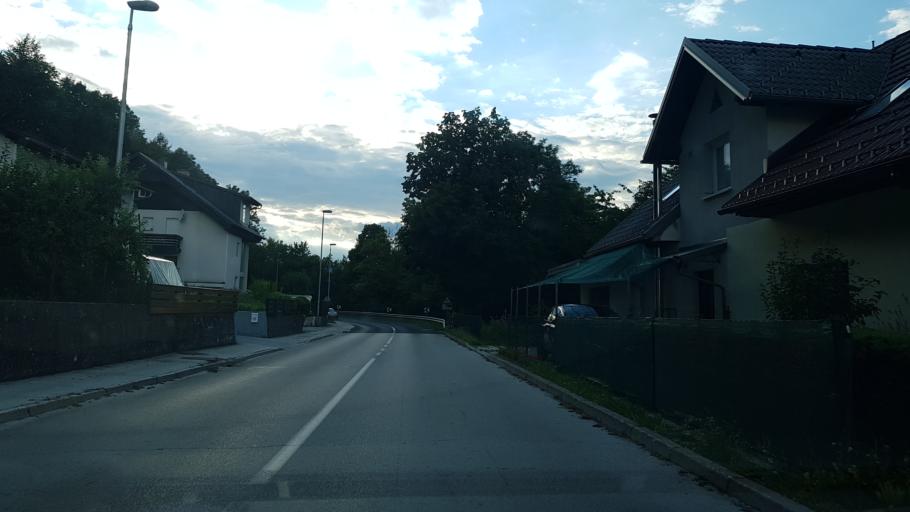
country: SI
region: Kranj
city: Kranj
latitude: 46.2478
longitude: 14.3383
